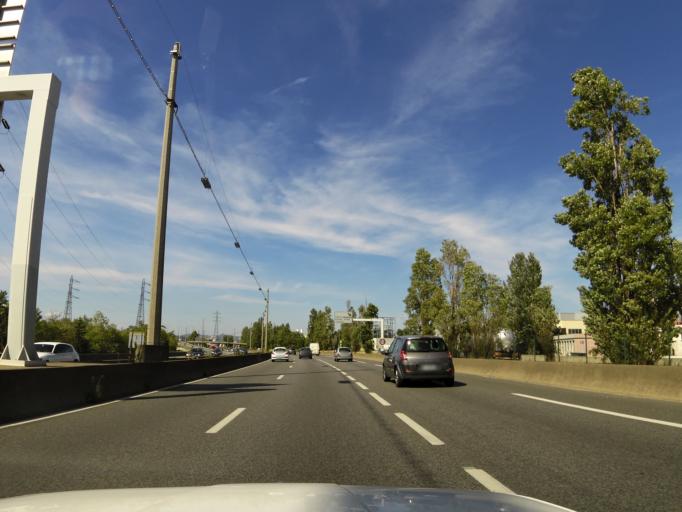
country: FR
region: Rhone-Alpes
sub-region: Departement du Rhone
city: Saint-Fons
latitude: 45.6999
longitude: 4.8457
